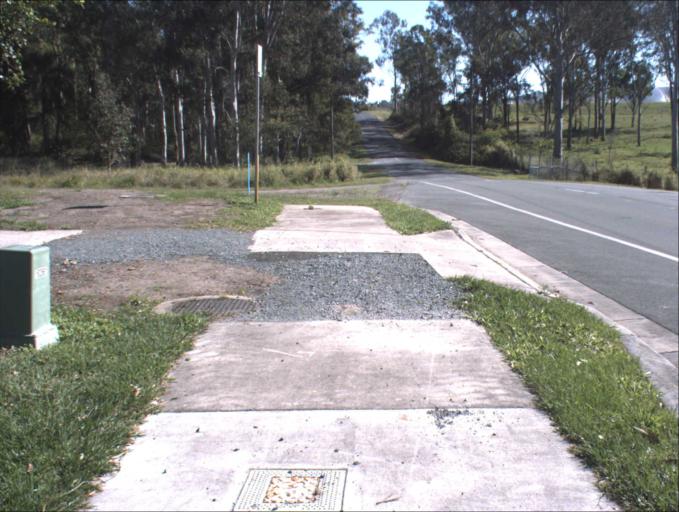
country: AU
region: Queensland
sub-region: Logan
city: Beenleigh
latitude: -27.7184
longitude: 153.1737
